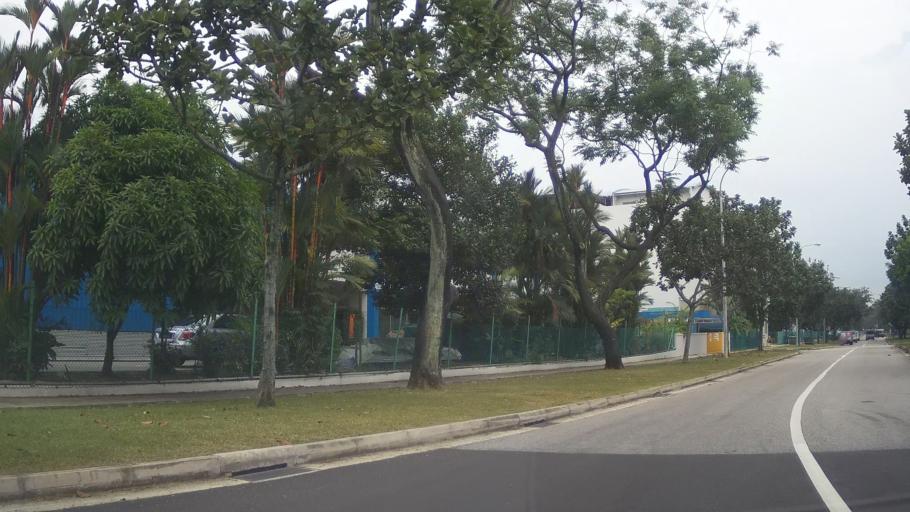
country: MY
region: Johor
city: Johor Bahru
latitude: 1.3333
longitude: 103.7017
